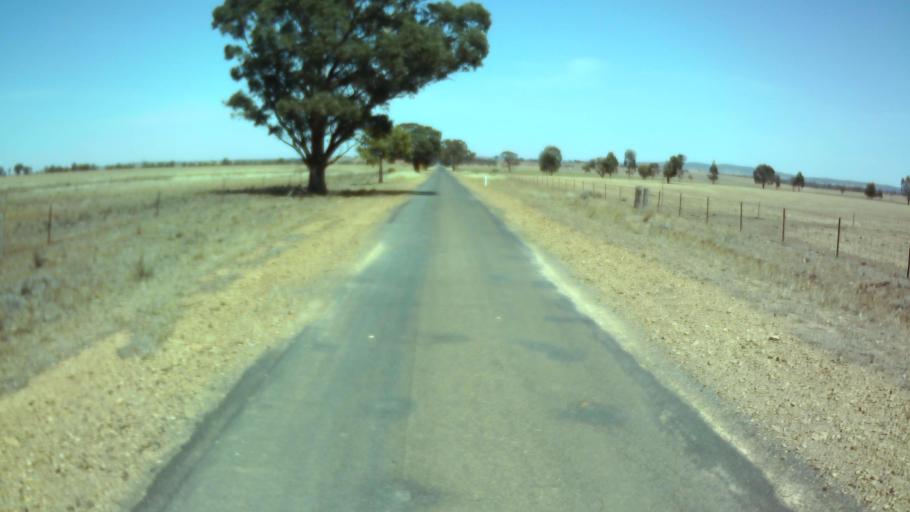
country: AU
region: New South Wales
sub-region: Weddin
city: Grenfell
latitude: -33.8596
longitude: 147.9748
